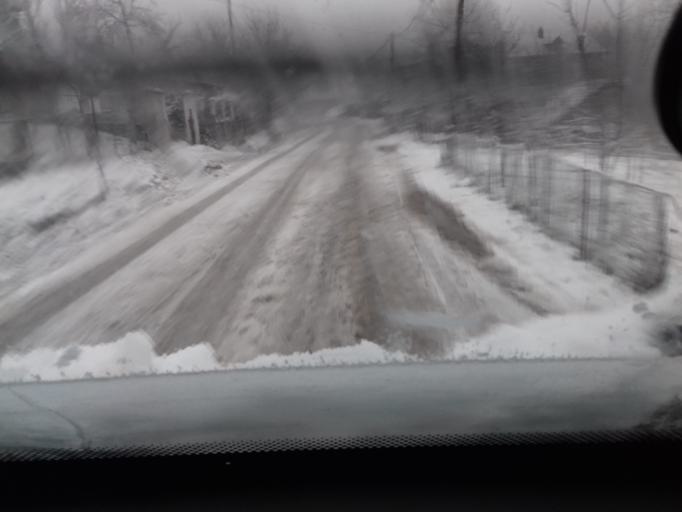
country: BA
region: Federation of Bosnia and Herzegovina
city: Lokvine
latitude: 44.2051
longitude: 17.8583
